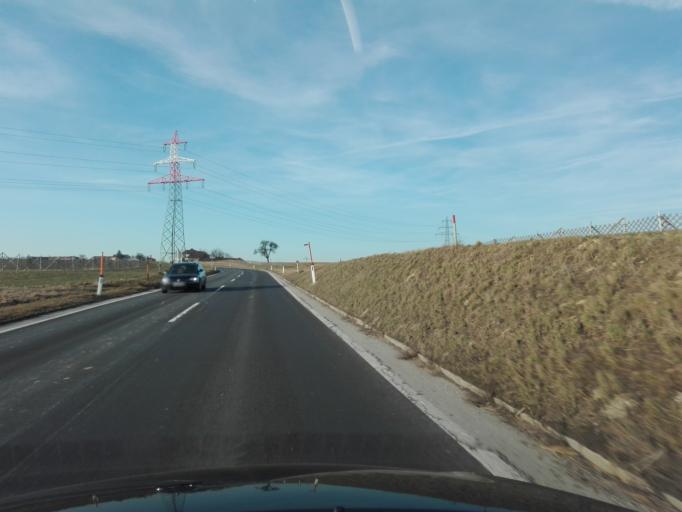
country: AT
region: Lower Austria
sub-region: Politischer Bezirk Amstetten
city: Strengberg
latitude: 48.1521
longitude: 14.6239
